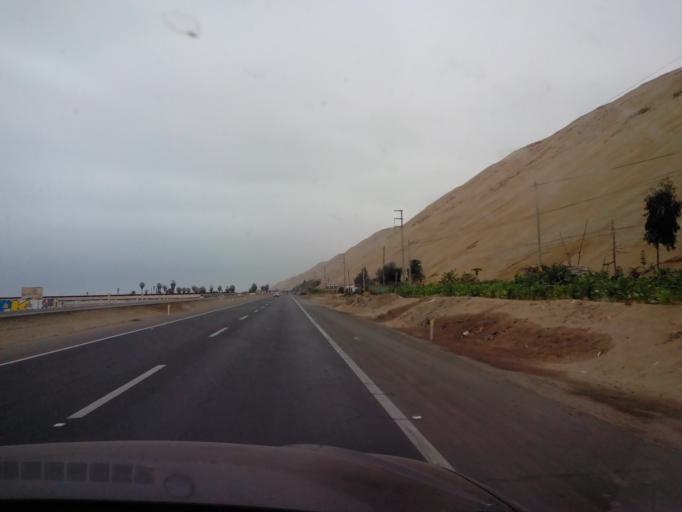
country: PE
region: Ica
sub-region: Provincia de Chincha
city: San Pedro
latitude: -13.3530
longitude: -76.2218
